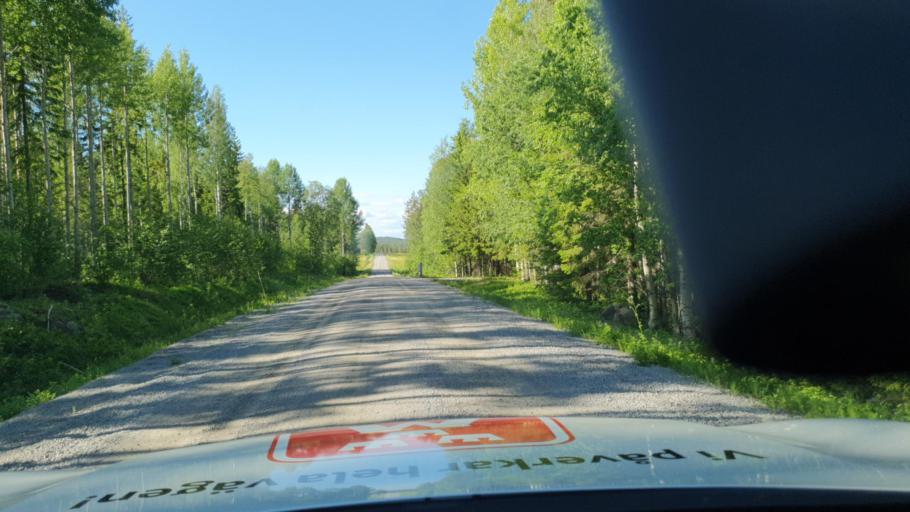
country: SE
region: Vaesterbotten
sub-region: Vannas Kommun
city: Vaennaes
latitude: 63.8058
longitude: 19.6391
